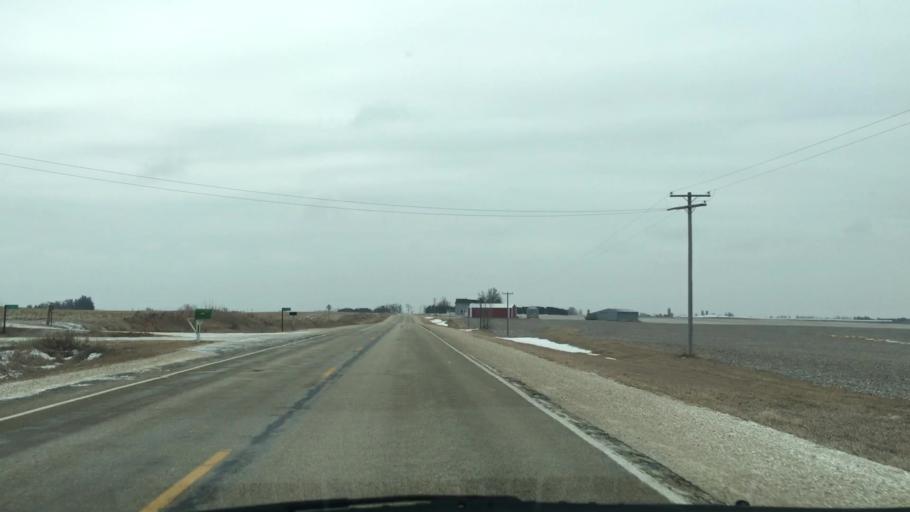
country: US
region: Iowa
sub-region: Fayette County
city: West Union
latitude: 43.0318
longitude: -91.8352
